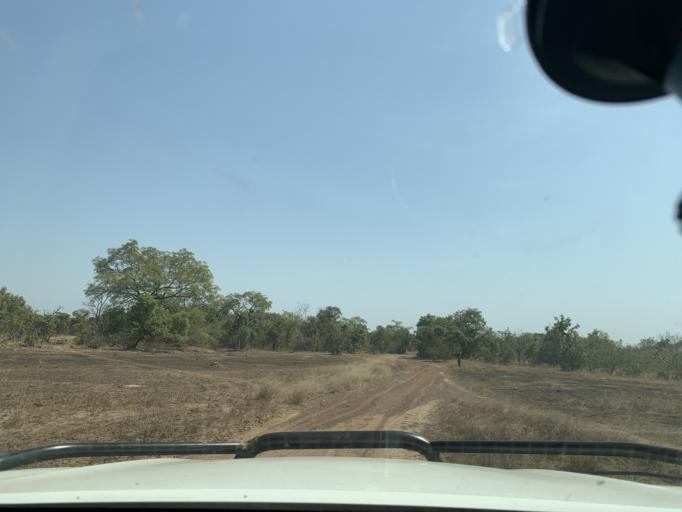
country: ML
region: Sikasso
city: Kolondieba
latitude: 10.8366
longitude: -6.7943
